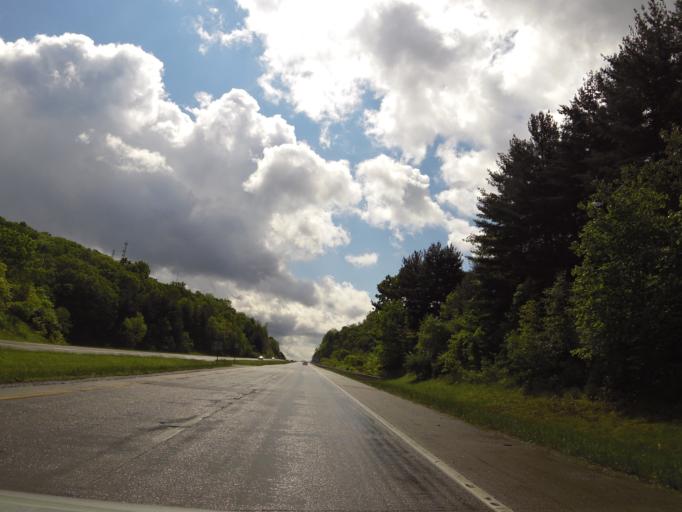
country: US
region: Ohio
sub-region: Athens County
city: Athens
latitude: 39.3565
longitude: -82.0981
